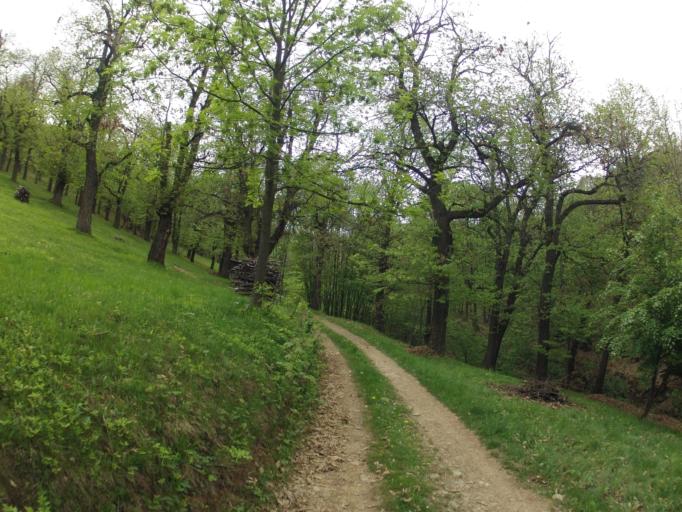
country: IT
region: Piedmont
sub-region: Provincia di Cuneo
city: Peveragno
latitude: 44.3181
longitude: 7.5854
